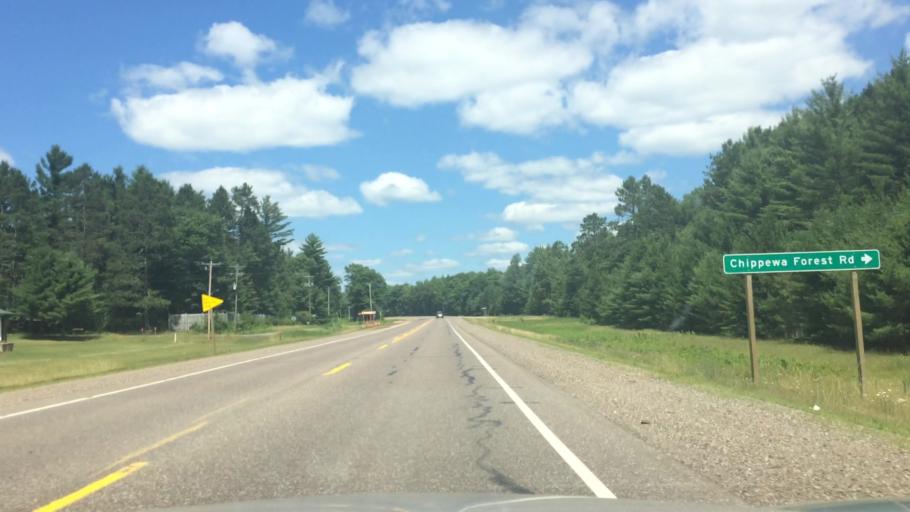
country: US
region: Wisconsin
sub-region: Vilas County
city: Lac du Flambeau
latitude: 45.9379
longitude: -89.6965
